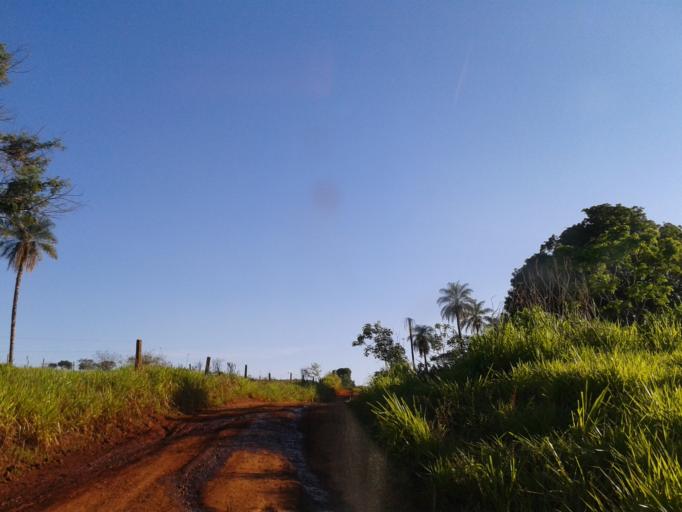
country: BR
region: Minas Gerais
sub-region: Centralina
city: Centralina
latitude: -18.6845
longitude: -49.2831
